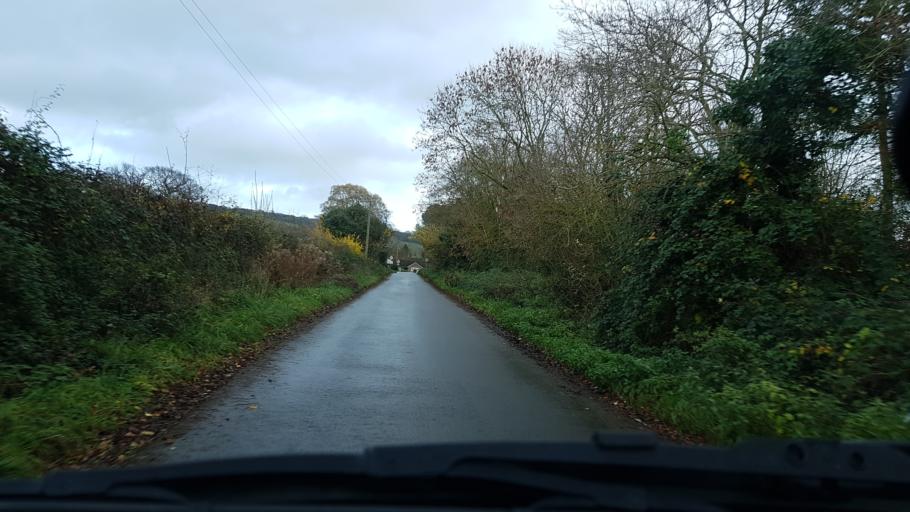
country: GB
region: England
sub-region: Worcestershire
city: Bredon
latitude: 52.0505
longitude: -2.1066
